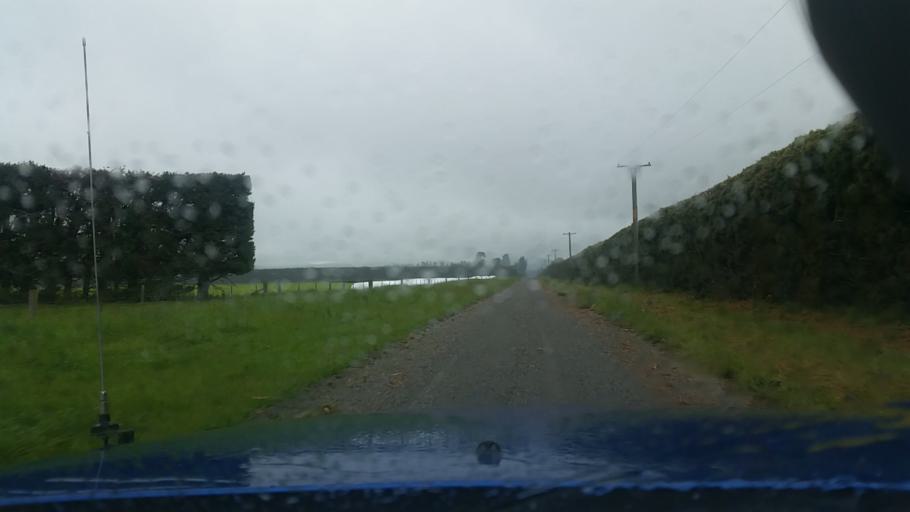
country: NZ
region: Canterbury
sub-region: Ashburton District
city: Methven
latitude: -43.7581
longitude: 171.2629
